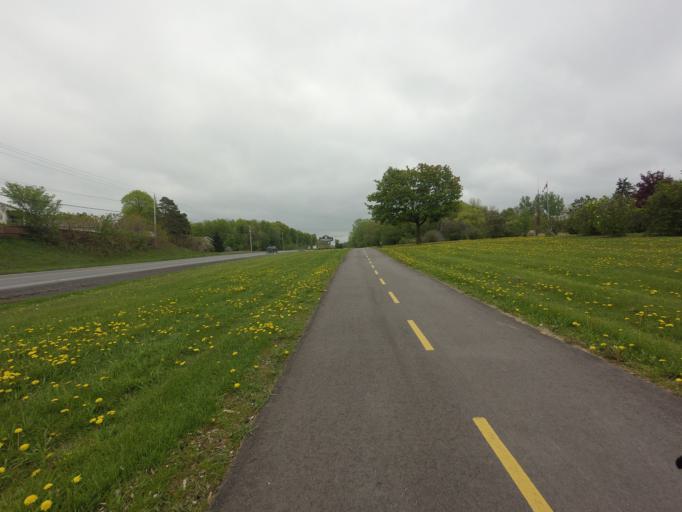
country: CA
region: Ontario
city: Cornwall
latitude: 45.0333
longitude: -74.8240
